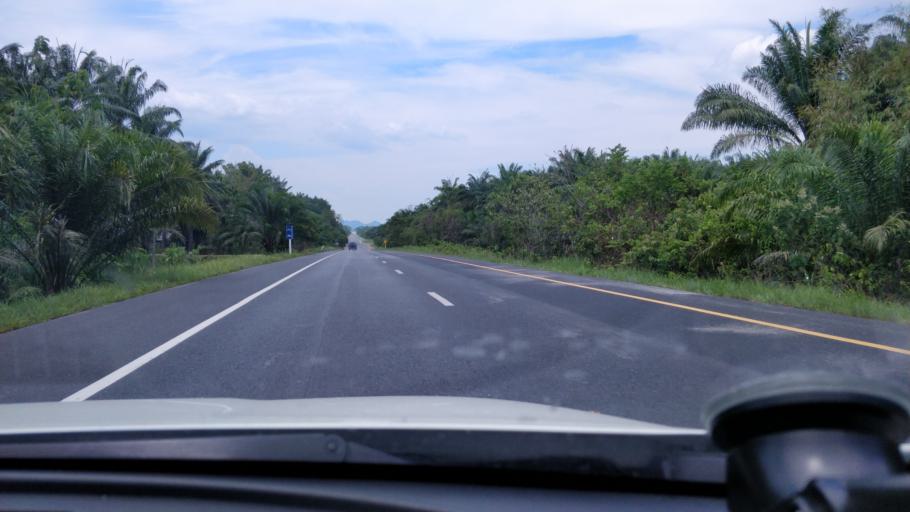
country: TH
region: Krabi
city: Plai Phraya
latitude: 8.4900
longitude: 98.8774
